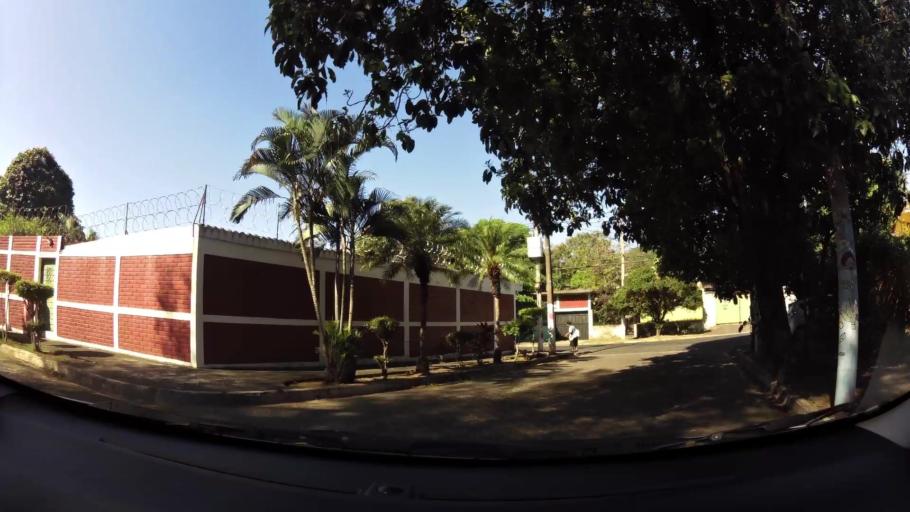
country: SV
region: Sonsonate
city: Sonzacate
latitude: 13.7297
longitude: -89.7207
